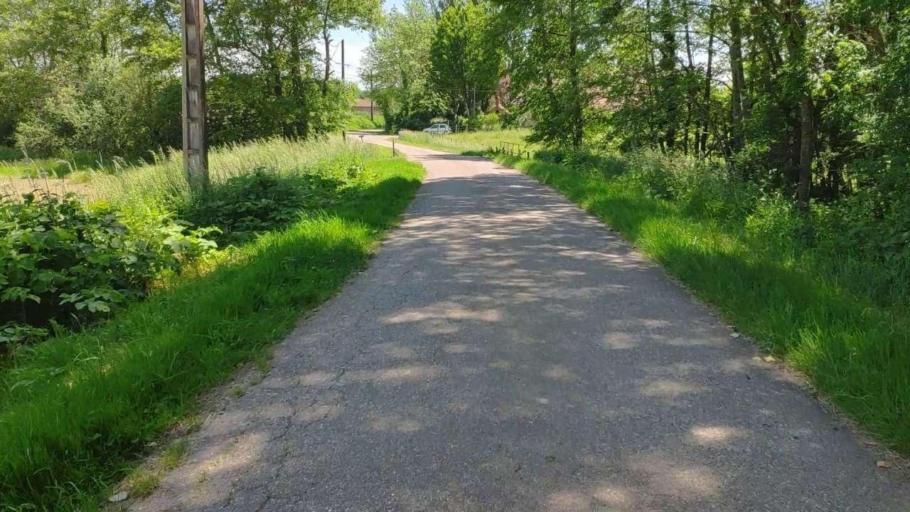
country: FR
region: Franche-Comte
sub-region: Departement du Jura
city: Bletterans
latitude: 46.7915
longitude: 5.3937
